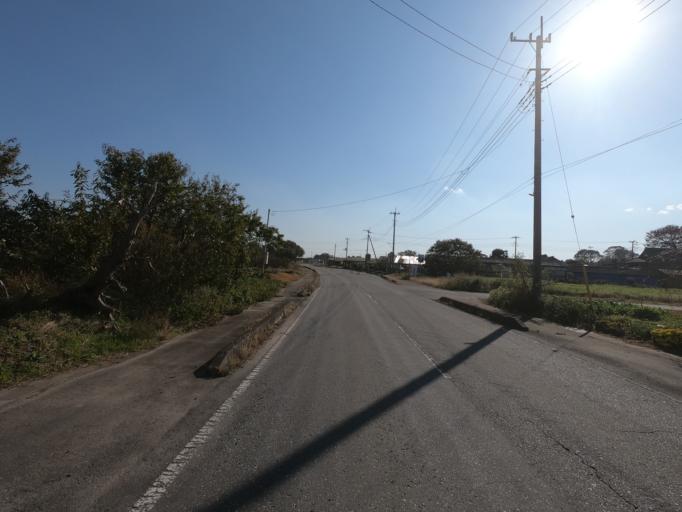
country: JP
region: Ibaraki
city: Tsukuba
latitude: 36.1347
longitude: 140.1492
